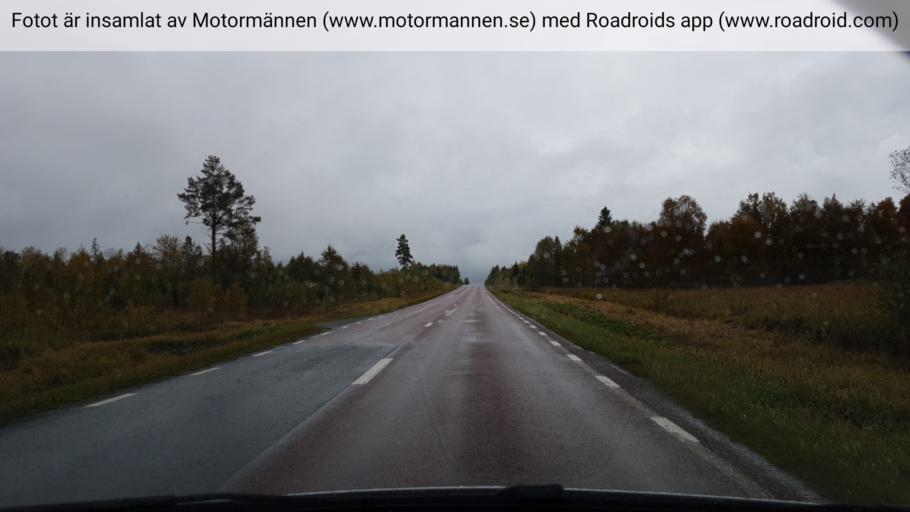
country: SE
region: Jaemtland
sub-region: Stroemsunds Kommun
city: Stroemsund
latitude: 63.7801
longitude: 15.5085
